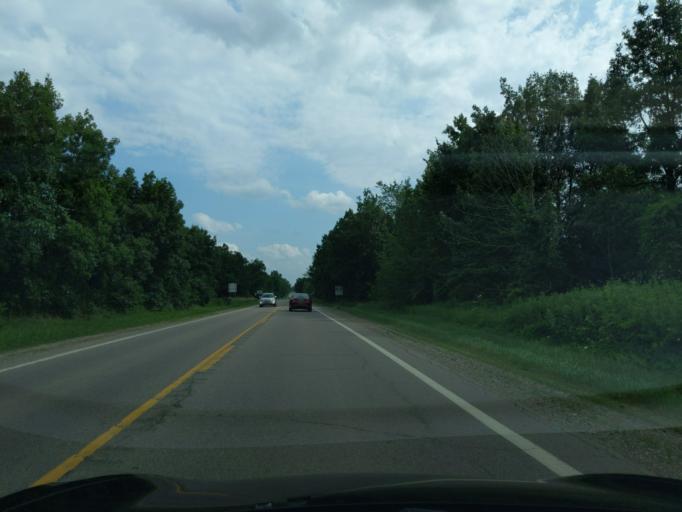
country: US
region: Michigan
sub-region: Eaton County
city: Eaton Rapids
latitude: 42.4364
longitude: -84.6497
